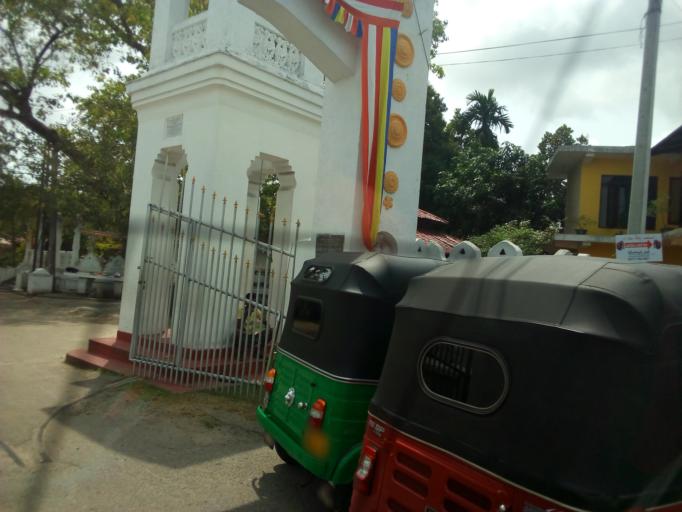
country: LK
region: Western
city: Galkissa
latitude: 6.8371
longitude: 79.8857
